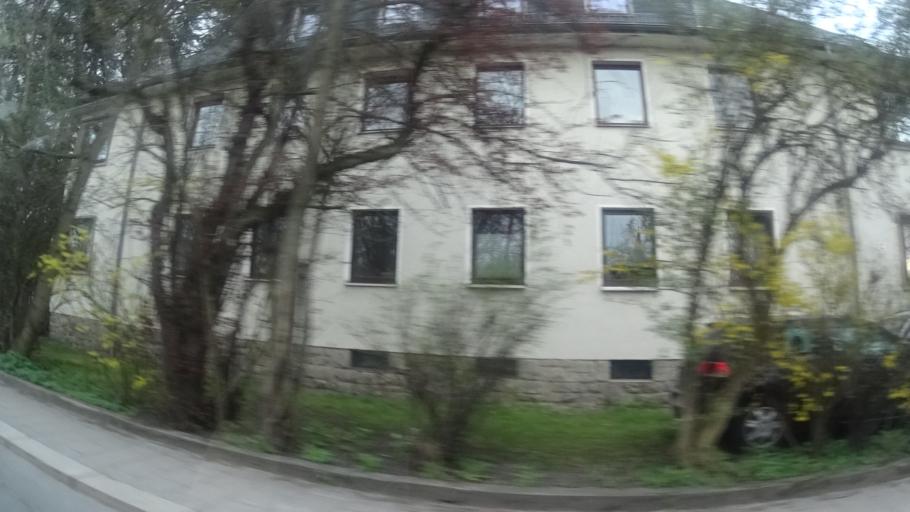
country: DE
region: Bavaria
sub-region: Upper Franconia
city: Hof
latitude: 50.3214
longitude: 11.9229
